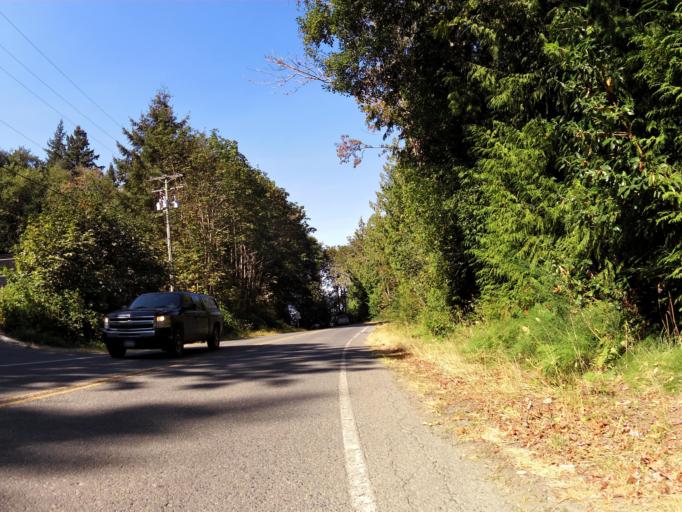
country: CA
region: British Columbia
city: North Saanich
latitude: 48.6179
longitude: -123.5223
